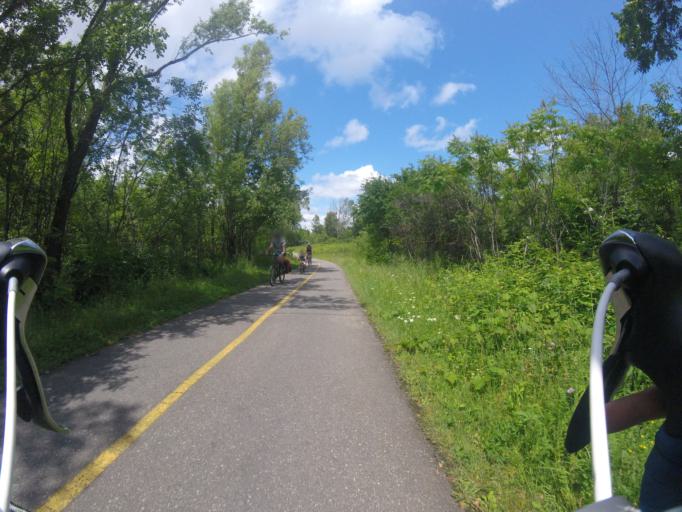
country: CA
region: Ontario
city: Ottawa
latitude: 45.4212
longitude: -75.7291
